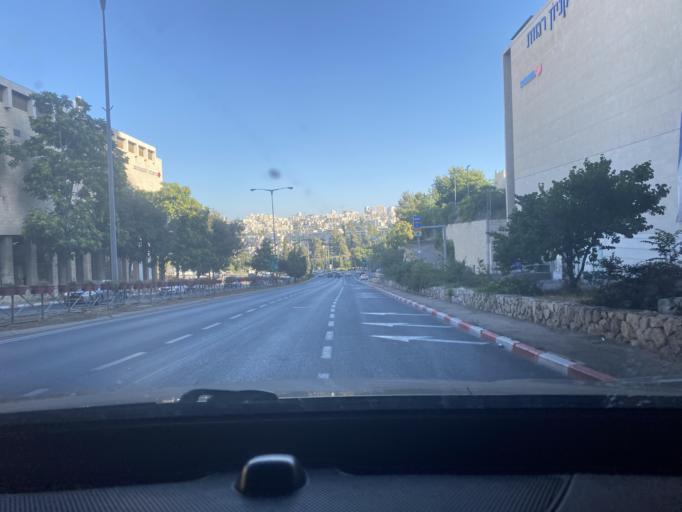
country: PS
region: West Bank
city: Bayt Iksa
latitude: 31.8173
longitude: 35.1952
